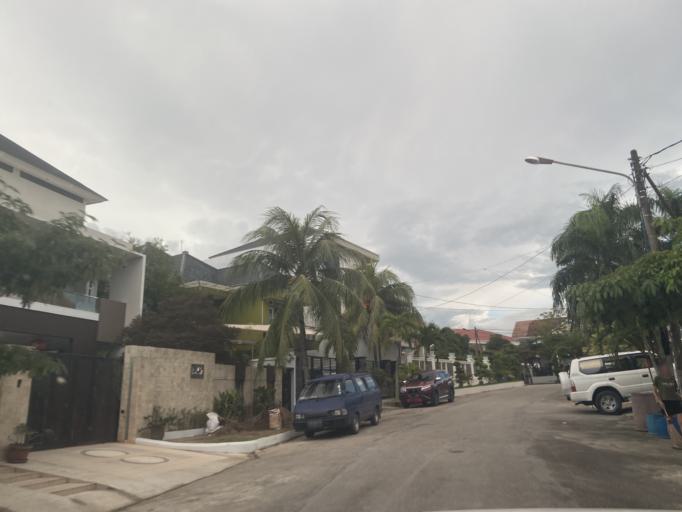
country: SG
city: Singapore
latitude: 1.1208
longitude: 104.0217
